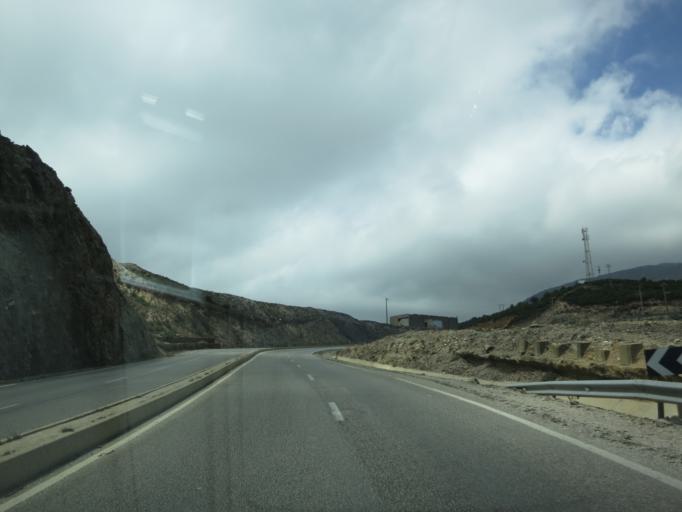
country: ES
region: Ceuta
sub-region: Ceuta
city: Ceuta
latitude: 35.8749
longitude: -5.3927
